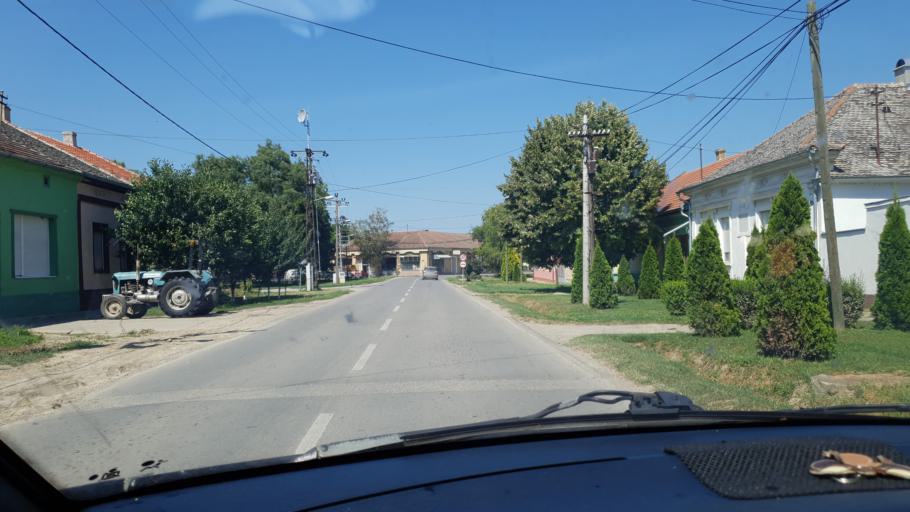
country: RS
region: Autonomna Pokrajina Vojvodina
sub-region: Juznobacki Okrug
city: Kovilj
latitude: 45.2290
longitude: 20.0221
